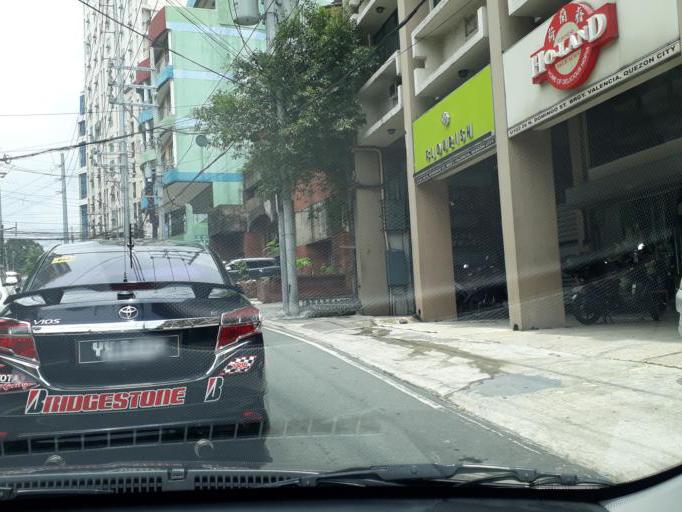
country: PH
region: Metro Manila
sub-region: San Juan
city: San Juan
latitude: 14.6115
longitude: 121.0351
